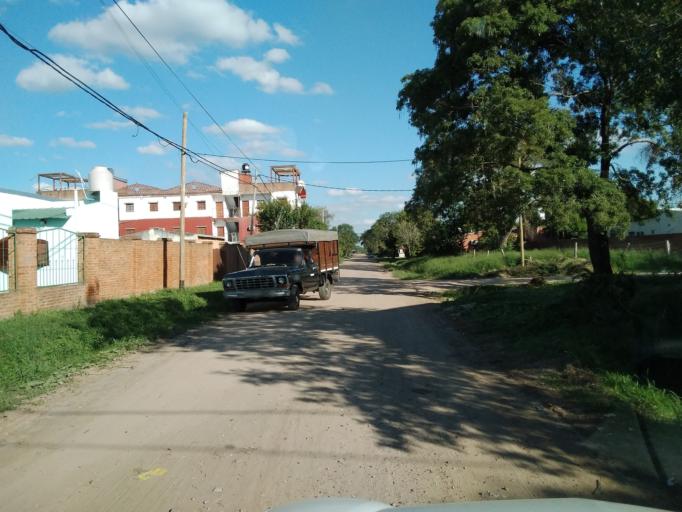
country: AR
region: Corrientes
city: Corrientes
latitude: -27.4608
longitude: -58.7772
